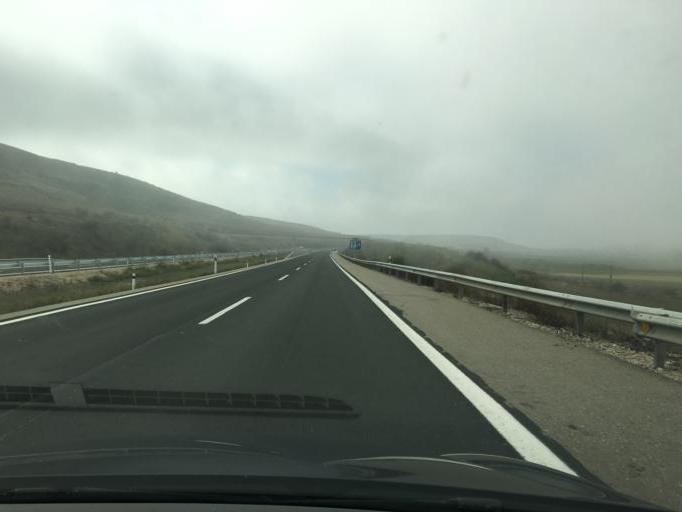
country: ES
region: Castille and Leon
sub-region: Provincia de Burgos
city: Villanueva de Teba
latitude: 42.6247
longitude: -3.1570
